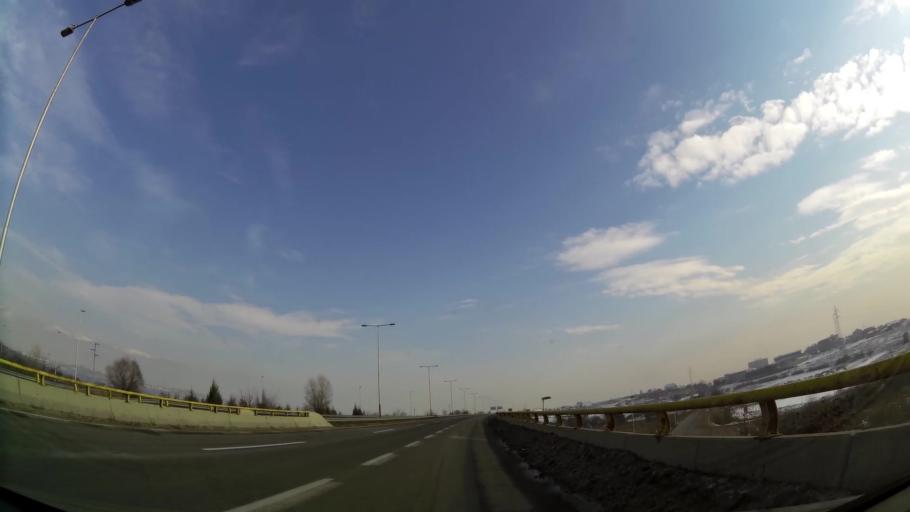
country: MK
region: Suto Orizari
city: Suto Orizare
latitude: 42.0526
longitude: 21.4221
